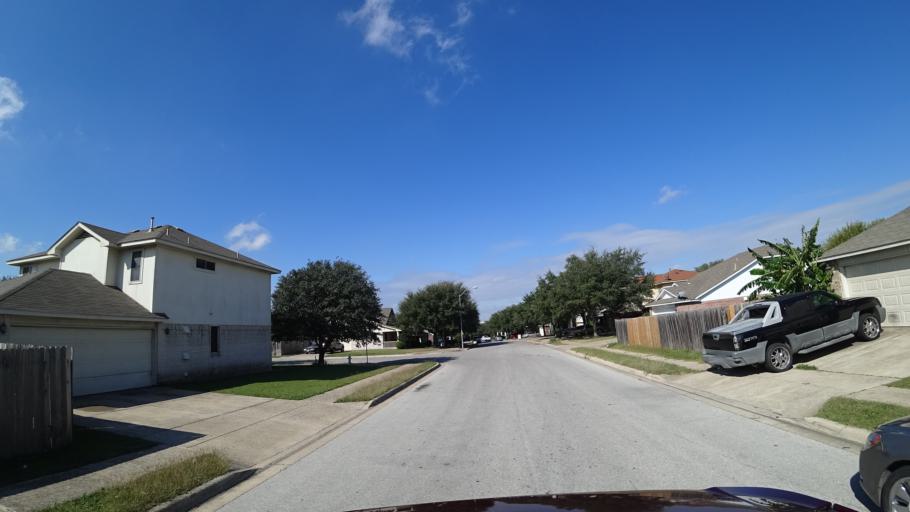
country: US
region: Texas
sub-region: Travis County
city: Windemere
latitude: 30.4452
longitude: -97.6543
